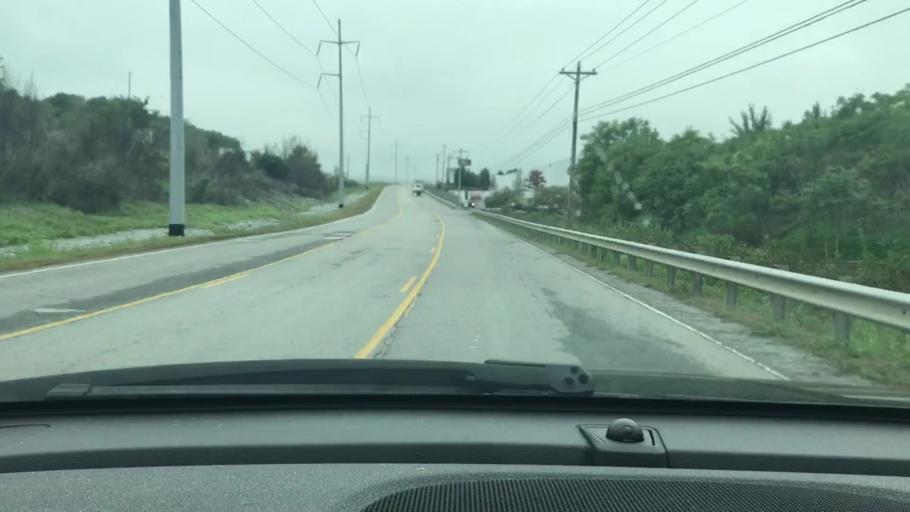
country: US
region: Tennessee
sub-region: Rutherford County
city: La Vergne
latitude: 35.9875
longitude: -86.5834
